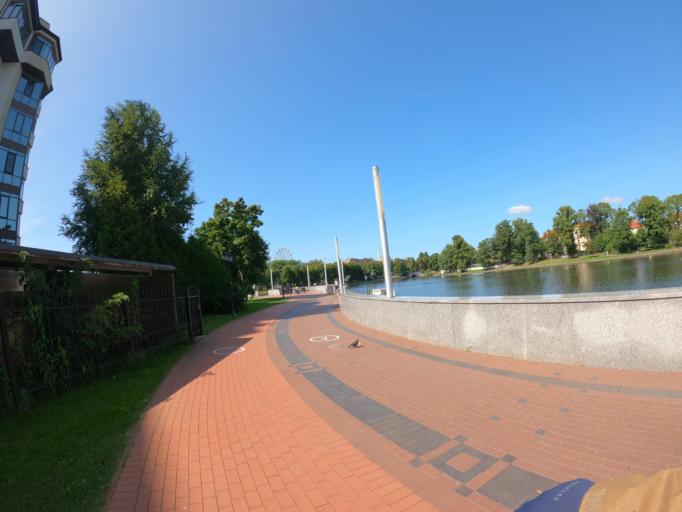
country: RU
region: Kaliningrad
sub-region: Gorod Kaliningrad
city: Kaliningrad
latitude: 54.7284
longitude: 20.5216
